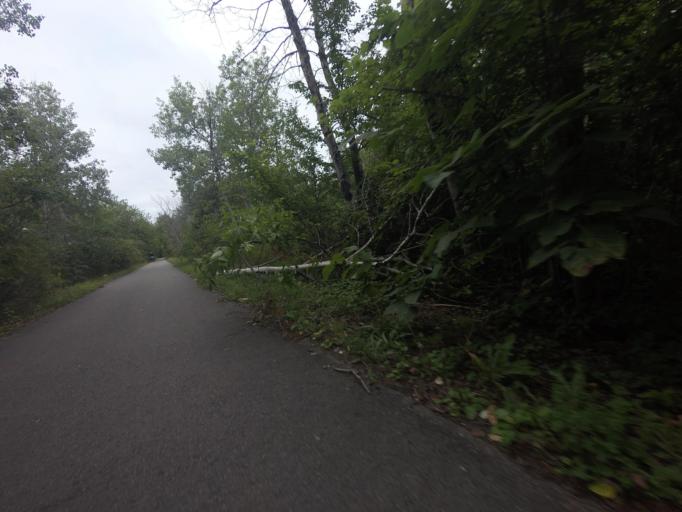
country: CA
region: Ontario
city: Omemee
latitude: 44.3781
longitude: -78.7495
